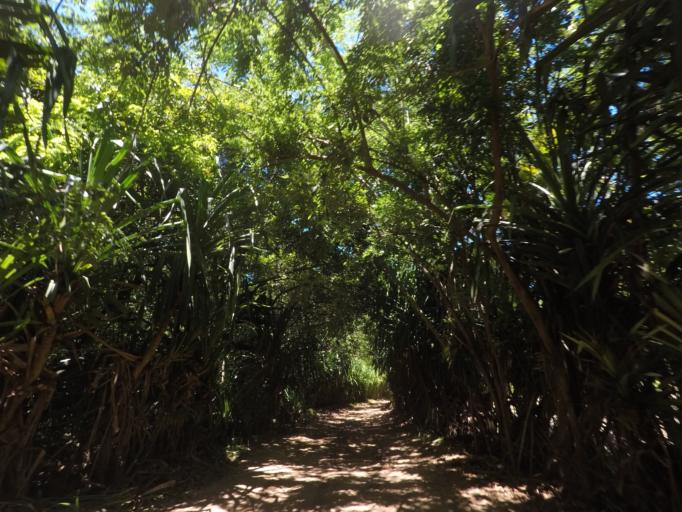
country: BR
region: Bahia
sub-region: Marau
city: Marau
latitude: -14.0228
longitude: -38.9492
